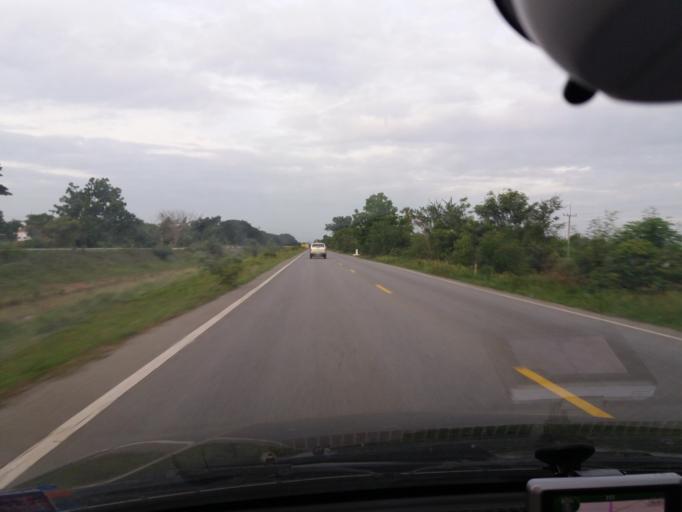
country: TH
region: Suphan Buri
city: Don Chedi
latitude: 14.5371
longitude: 99.9354
